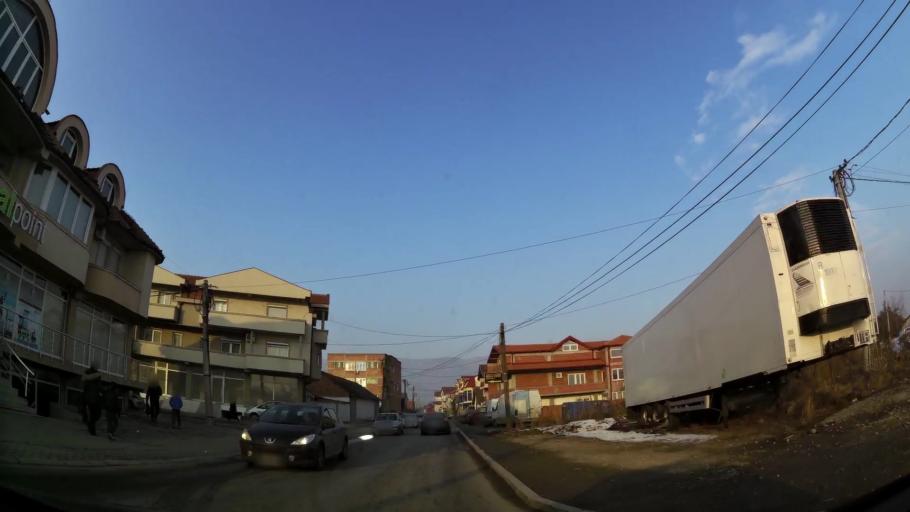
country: MK
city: Creshevo
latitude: 42.0163
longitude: 21.5123
